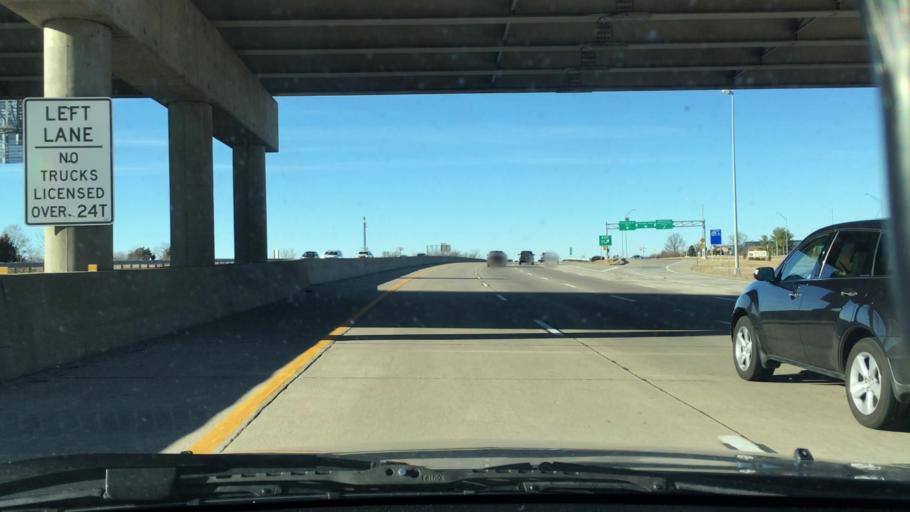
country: US
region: Missouri
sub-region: Saint Charles County
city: Weldon Spring
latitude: 38.7029
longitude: -90.6732
